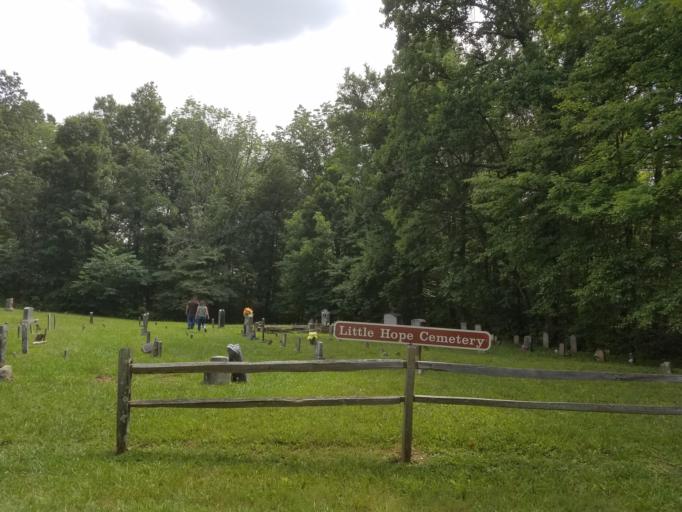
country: US
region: Kentucky
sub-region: Barren County
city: Cave City
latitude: 37.1537
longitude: -86.0566
